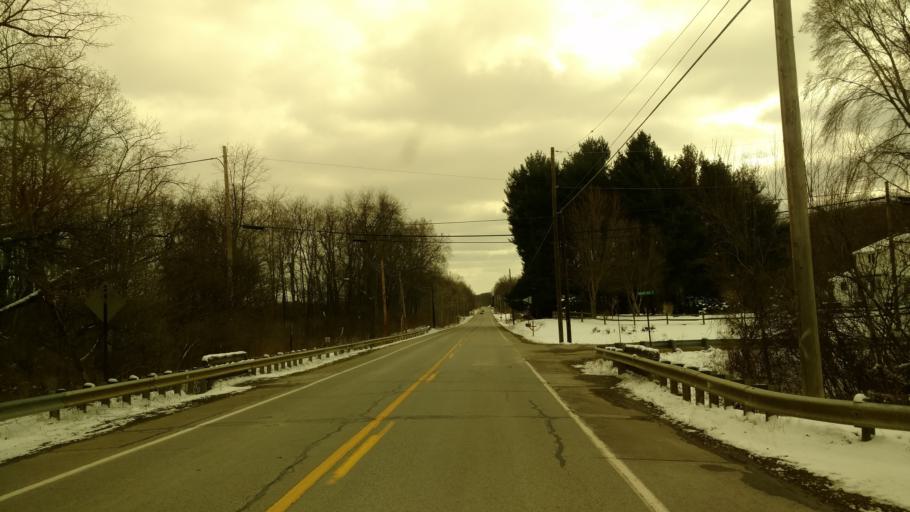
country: US
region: Pennsylvania
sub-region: Mercer County
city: Mercer
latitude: 41.2981
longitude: -80.2404
